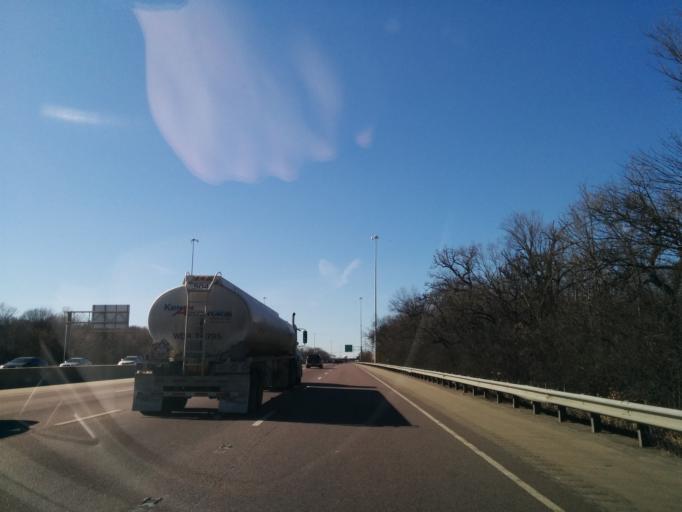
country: US
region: Illinois
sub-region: Cook County
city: Hodgkins
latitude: 41.7611
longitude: -87.8774
